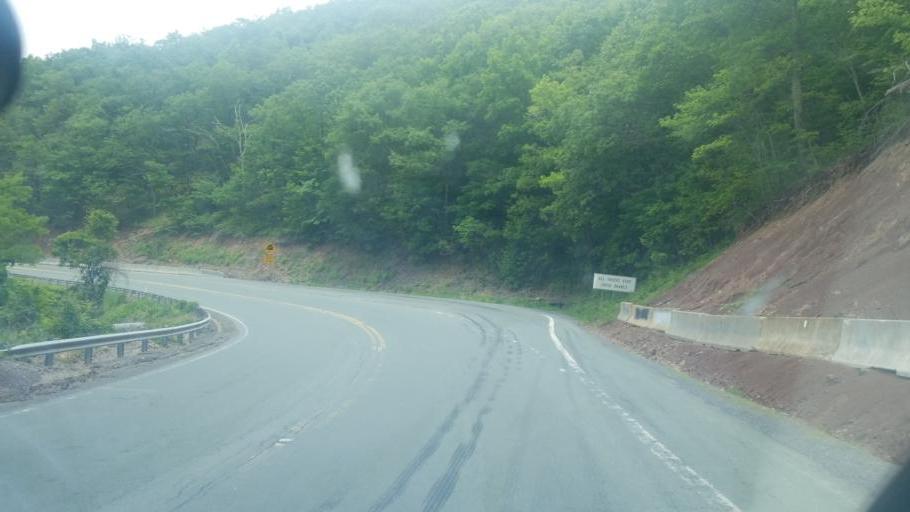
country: US
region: West Virginia
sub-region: Pendleton County
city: Franklin
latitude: 38.5848
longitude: -79.1657
